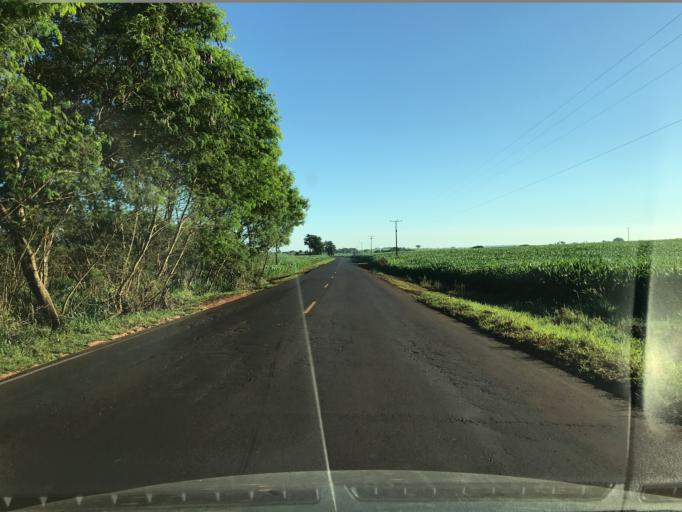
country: BR
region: Parana
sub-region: Palotina
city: Palotina
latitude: -24.1288
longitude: -53.8521
